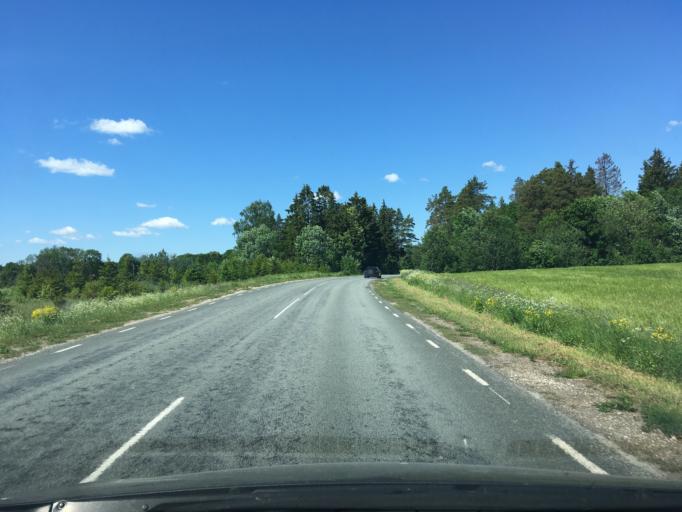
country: EE
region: Harju
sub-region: Rae vald
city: Vaida
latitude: 59.2011
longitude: 24.9580
